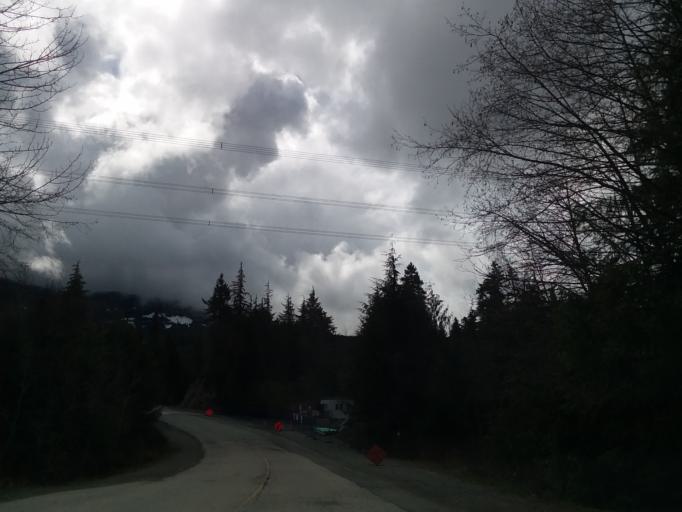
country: CA
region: British Columbia
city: Whistler
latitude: 50.0940
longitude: -123.0131
